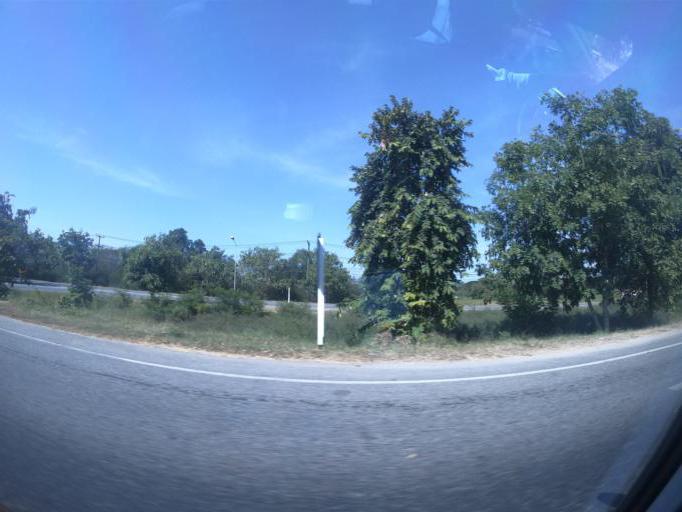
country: TH
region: Khon Kaen
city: Khon Kaen
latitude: 16.3902
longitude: 102.8097
